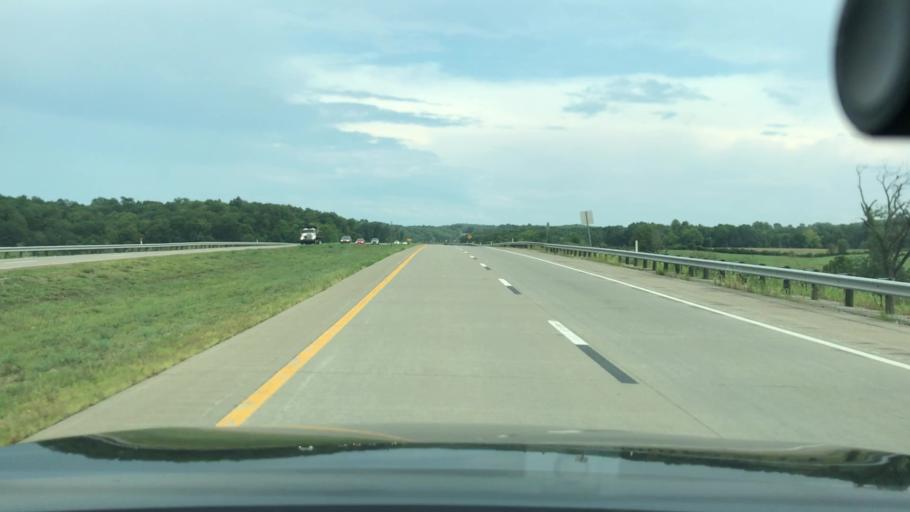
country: US
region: West Virginia
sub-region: Mason County
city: Point Pleasant
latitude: 38.7666
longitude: -82.0265
